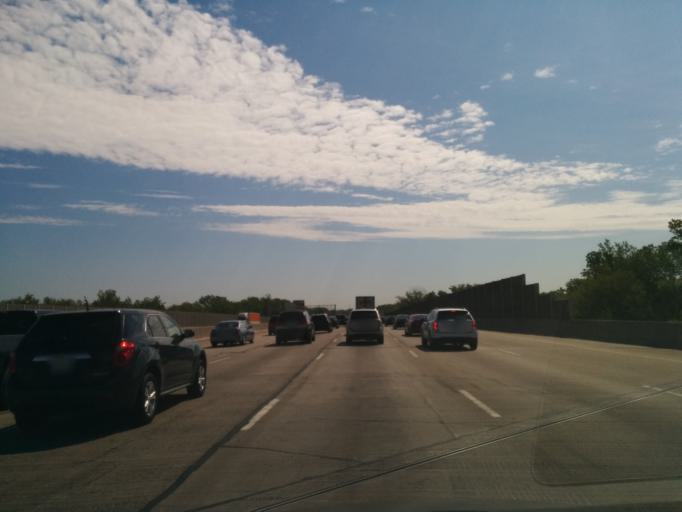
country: US
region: Indiana
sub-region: Lake County
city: New Chicago
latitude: 41.5723
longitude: -87.2829
